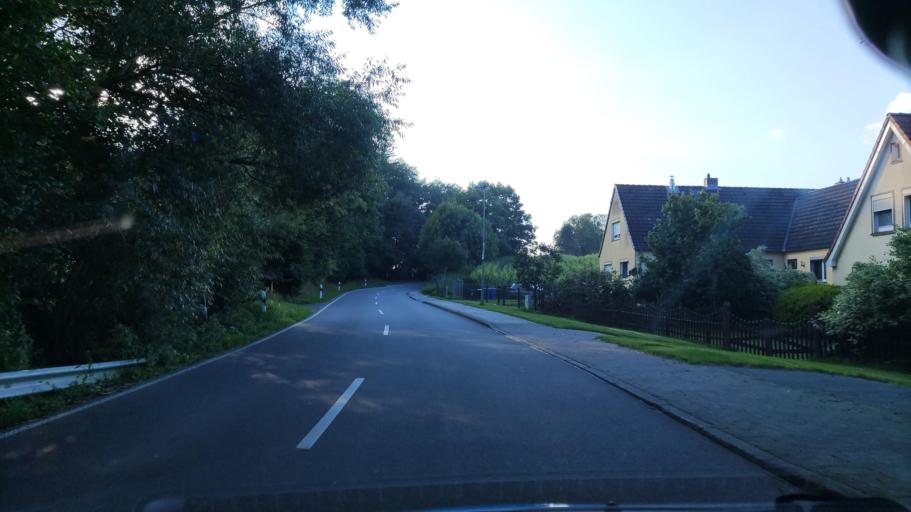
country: DE
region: Schleswig-Holstein
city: Glasau
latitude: 54.0590
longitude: 10.5227
